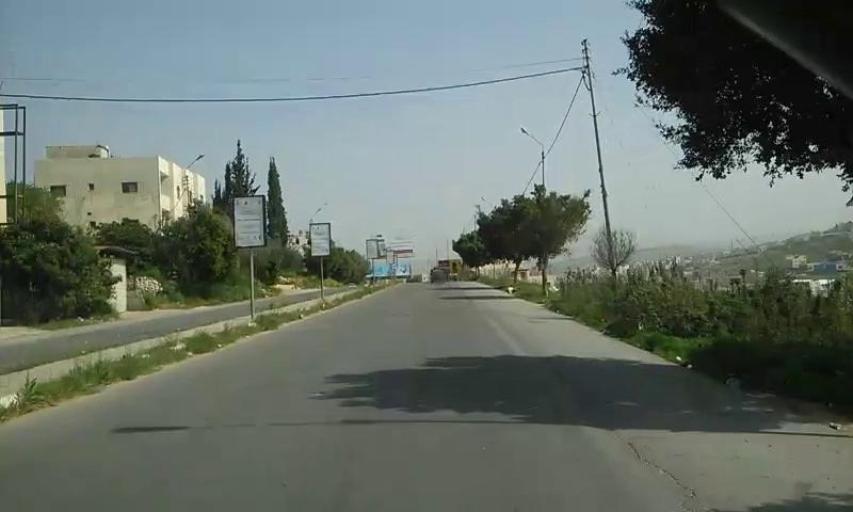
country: PS
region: West Bank
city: Kafr Qallil
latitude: 32.1848
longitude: 35.2788
